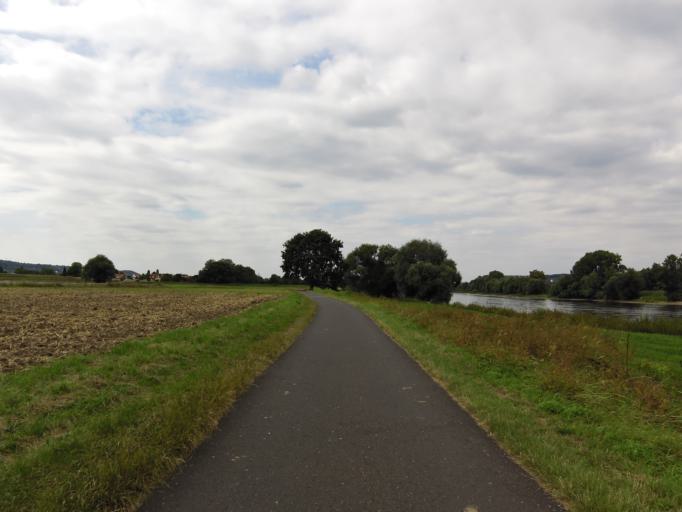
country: DE
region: Saxony
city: Radebeul
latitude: 51.0913
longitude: 13.6553
